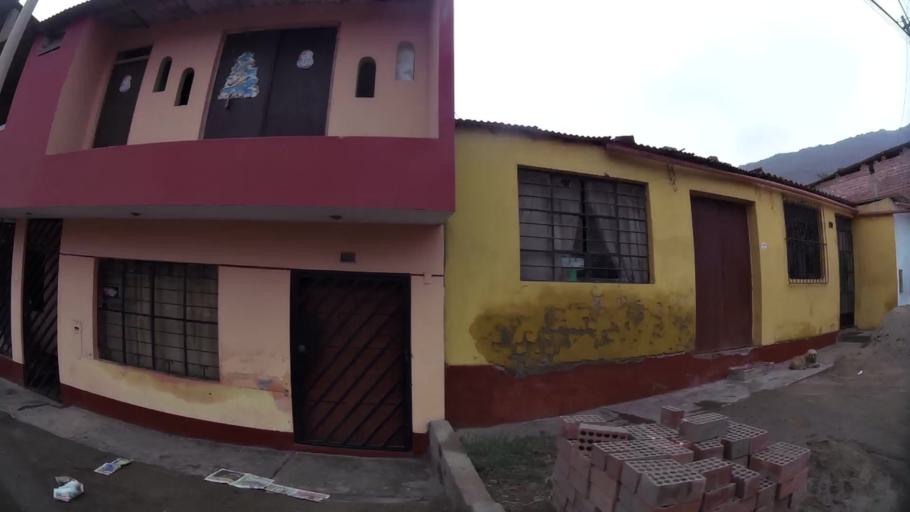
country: PE
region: Lima
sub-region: Lima
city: Surco
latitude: -12.2117
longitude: -76.9113
